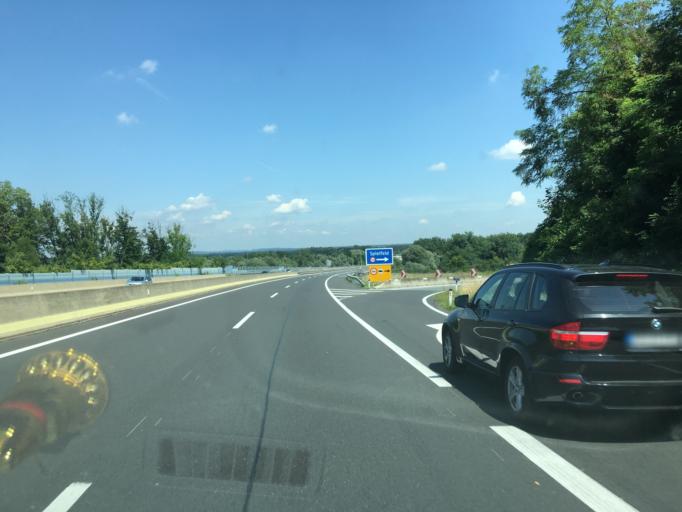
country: AT
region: Styria
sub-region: Politischer Bezirk Leibnitz
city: Spielfeld
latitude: 46.7043
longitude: 15.6384
